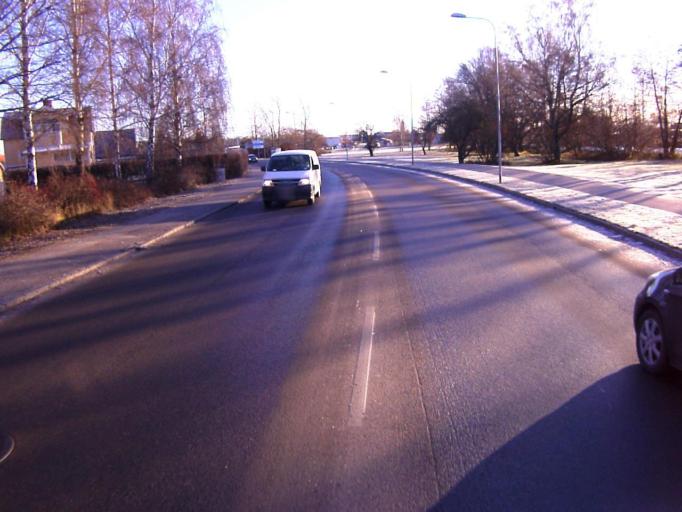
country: SE
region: Soedermanland
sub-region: Eskilstuna Kommun
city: Eskilstuna
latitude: 59.3830
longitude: 16.4960
